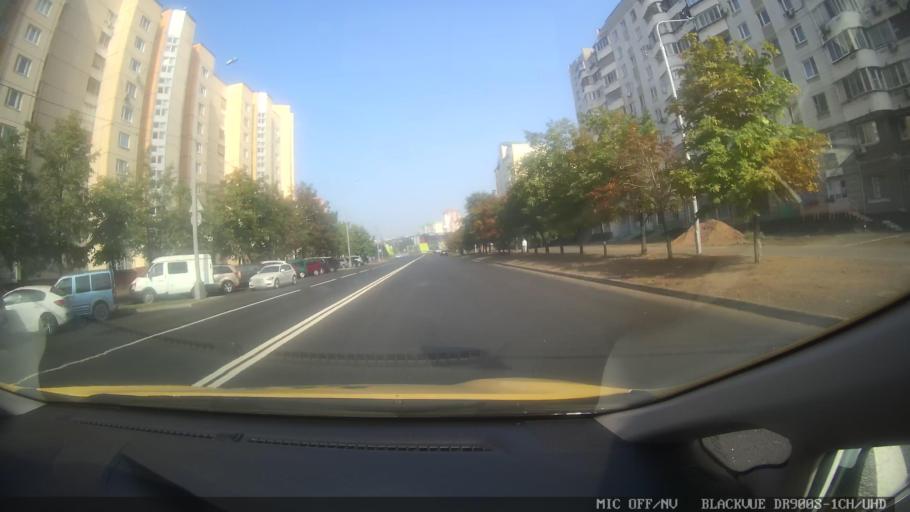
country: RU
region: Moscow
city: Zhulebino
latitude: 55.6822
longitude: 37.8563
